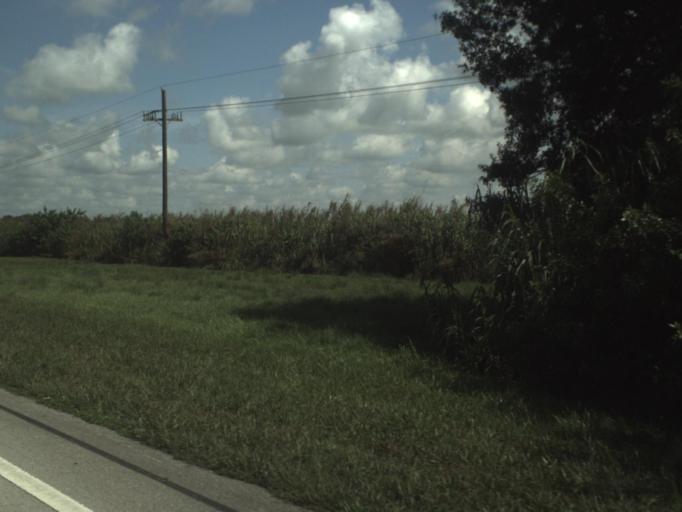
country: US
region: Florida
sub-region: Martin County
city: Indiantown
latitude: 27.0037
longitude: -80.4426
